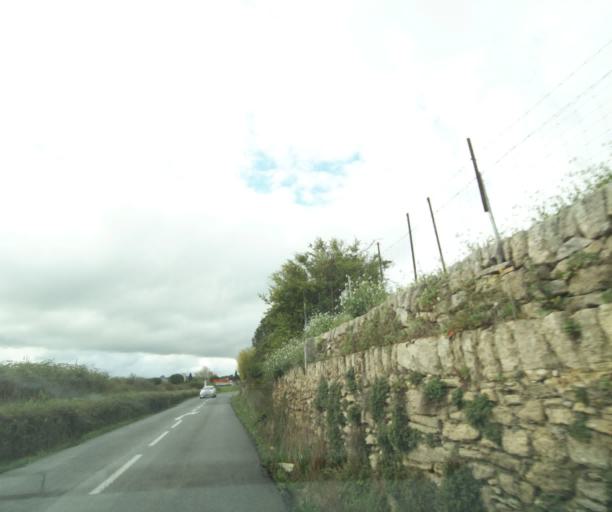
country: FR
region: Languedoc-Roussillon
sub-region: Departement de l'Herault
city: Saussan
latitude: 43.5780
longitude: 3.7687
